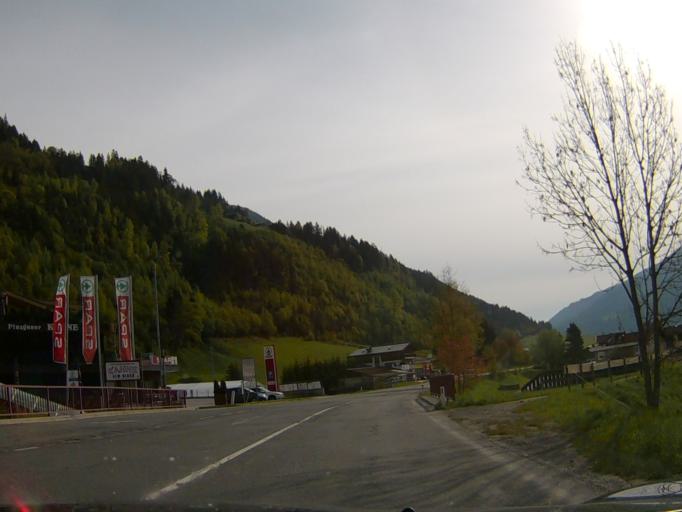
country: AT
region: Salzburg
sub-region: Politischer Bezirk Zell am See
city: Neukirchen am Grossvenediger
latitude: 47.2510
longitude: 12.2784
